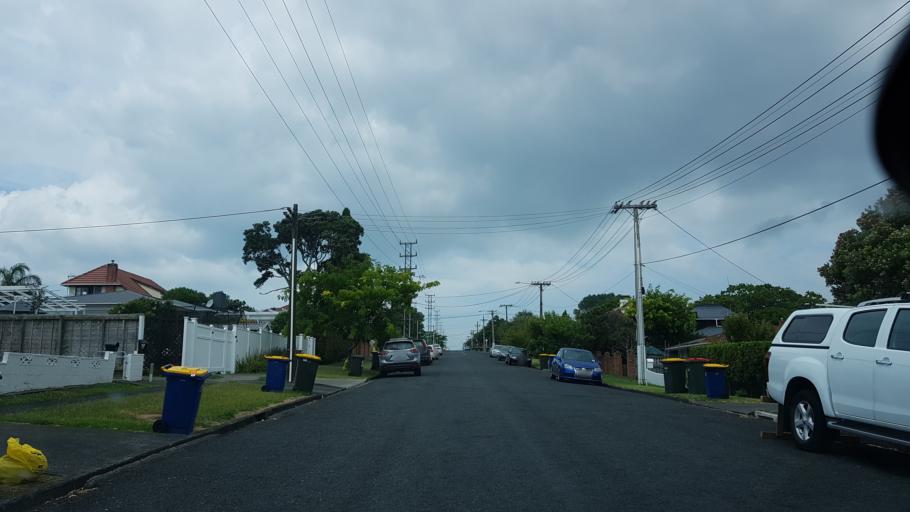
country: NZ
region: Auckland
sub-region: Auckland
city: North Shore
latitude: -36.7987
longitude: 174.7705
